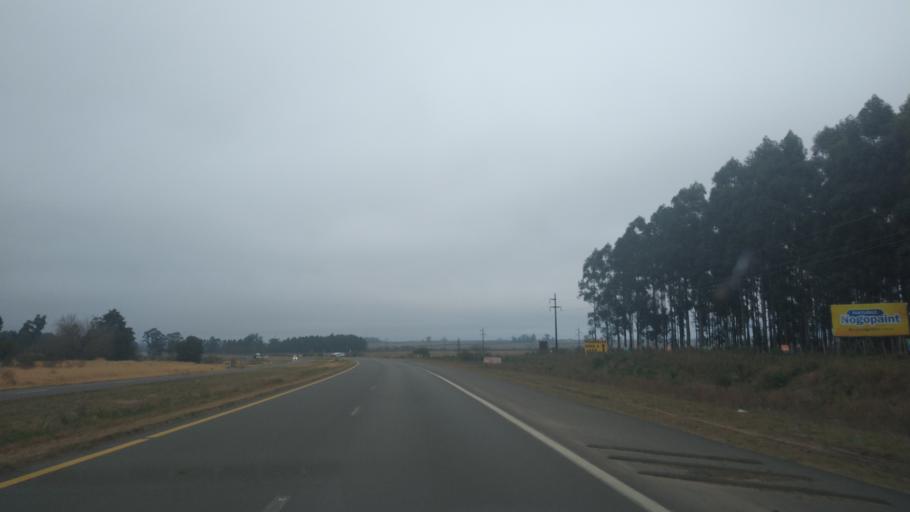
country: AR
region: Entre Rios
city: Chajari
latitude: -30.8279
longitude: -58.0482
